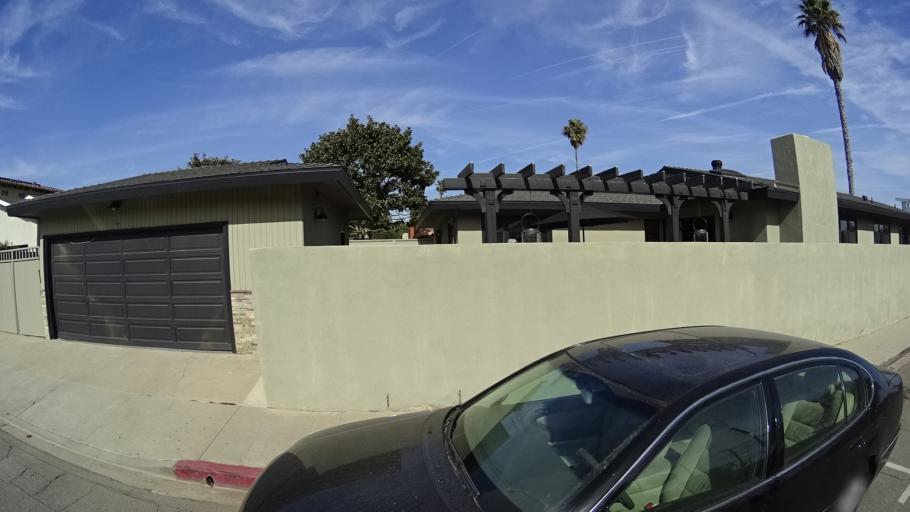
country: US
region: California
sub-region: Los Angeles County
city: Manhattan Beach
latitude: 33.8910
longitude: -118.3856
